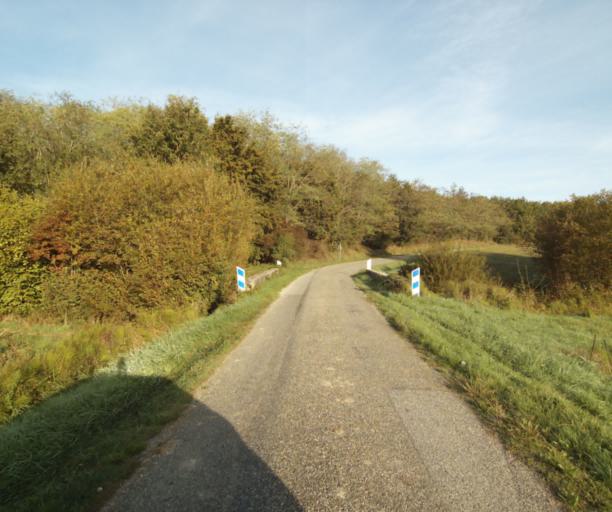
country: FR
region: Midi-Pyrenees
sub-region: Departement du Tarn-et-Garonne
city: Nohic
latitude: 43.9256
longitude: 1.4814
